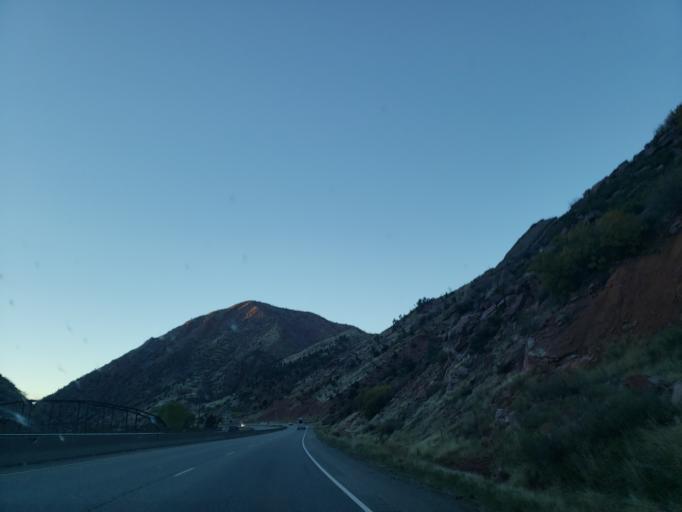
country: US
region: Colorado
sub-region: Garfield County
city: Glenwood Springs
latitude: 39.5610
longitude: -107.4058
